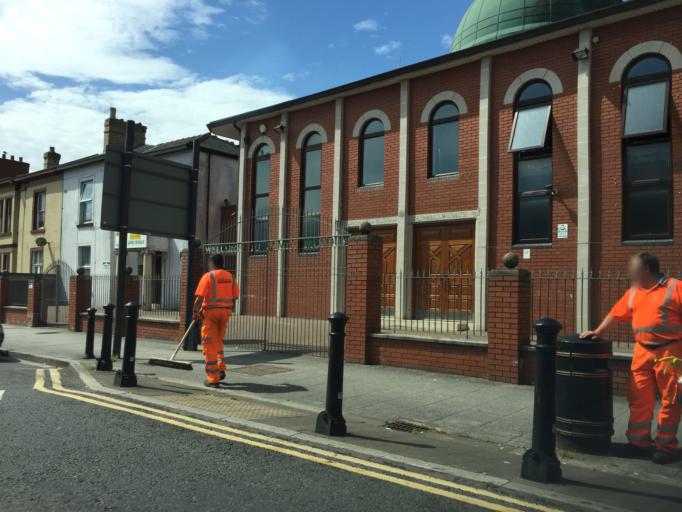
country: GB
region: Wales
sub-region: Newport
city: Newport
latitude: 51.5813
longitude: -2.9915
